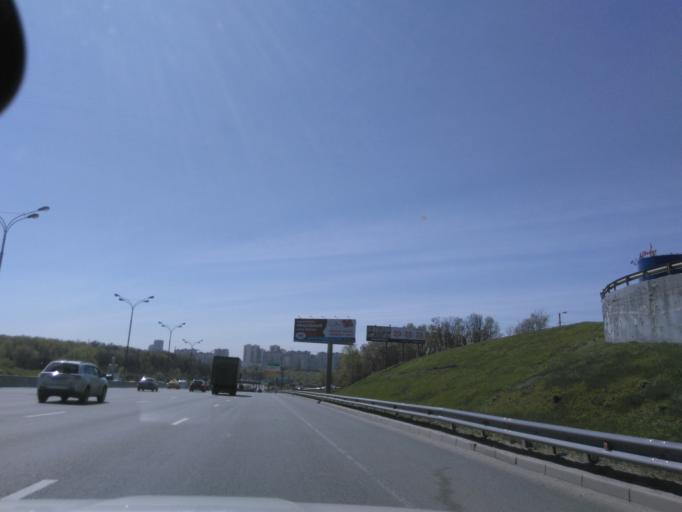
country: RU
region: Moscow
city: Strogino
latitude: 55.8569
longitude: 37.3962
